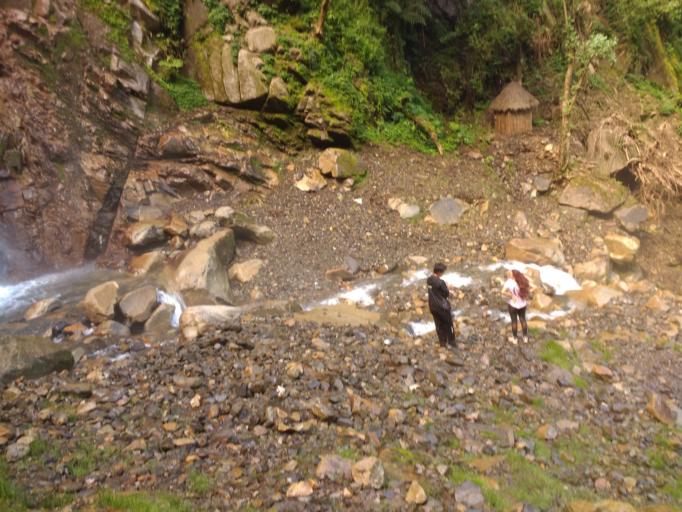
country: PE
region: Cusco
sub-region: Provincia de La Convencion
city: Maranura
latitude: -12.9689
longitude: -72.5287
